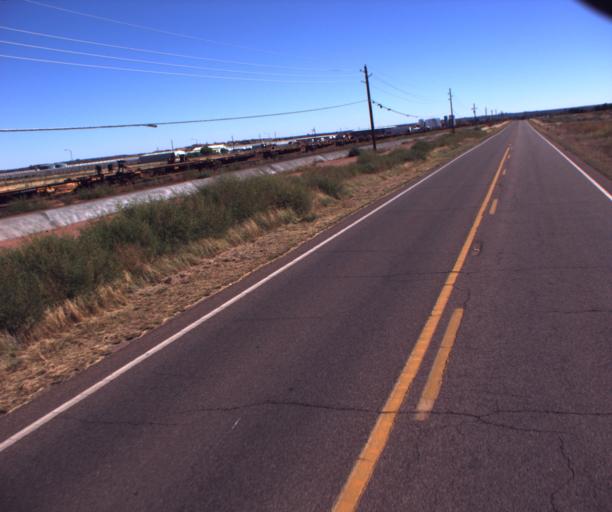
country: US
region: Arizona
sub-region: Navajo County
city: Snowflake
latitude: 34.5131
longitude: -110.1128
